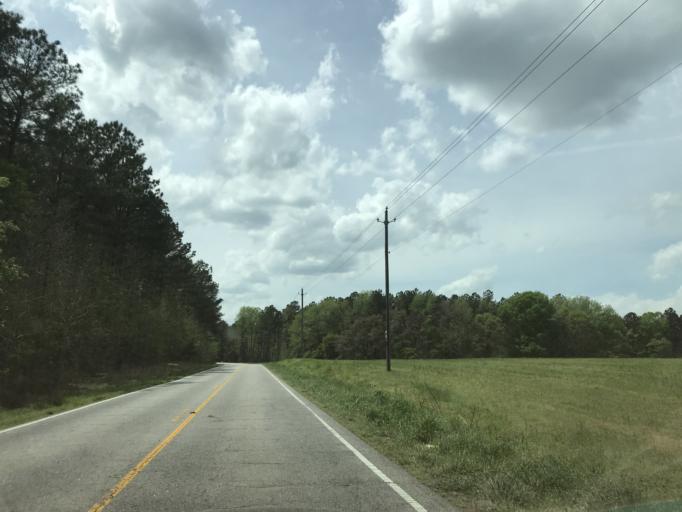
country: US
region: North Carolina
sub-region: Nash County
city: Spring Hope
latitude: 35.9695
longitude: -78.2130
